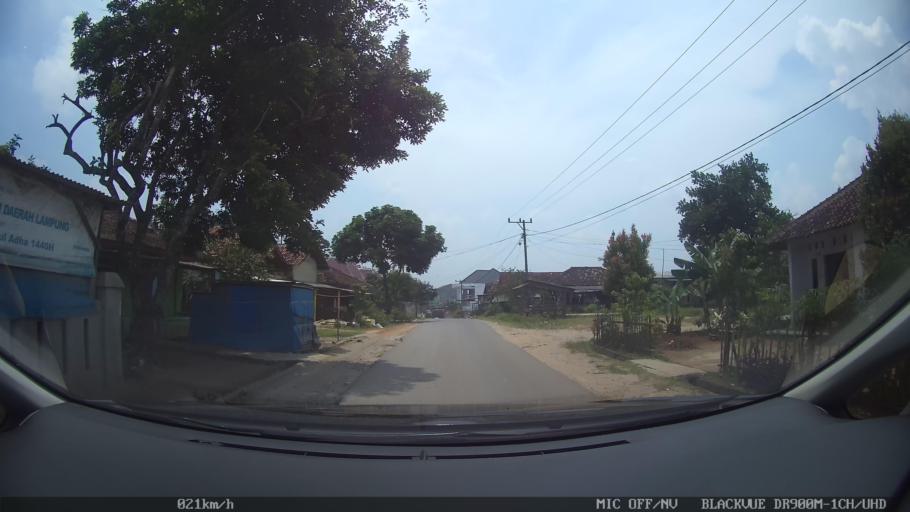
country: ID
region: Lampung
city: Kedaton
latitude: -5.3337
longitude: 105.2470
